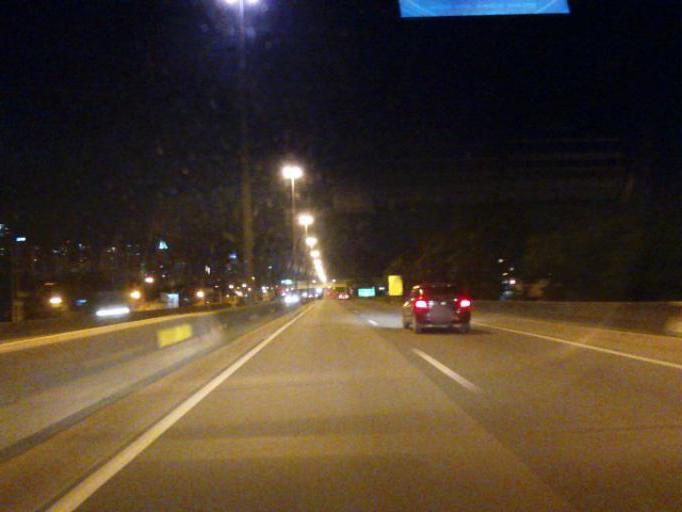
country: BR
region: Santa Catarina
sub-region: Balneario Camboriu
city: Balneario Camboriu
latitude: -27.0018
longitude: -48.6378
